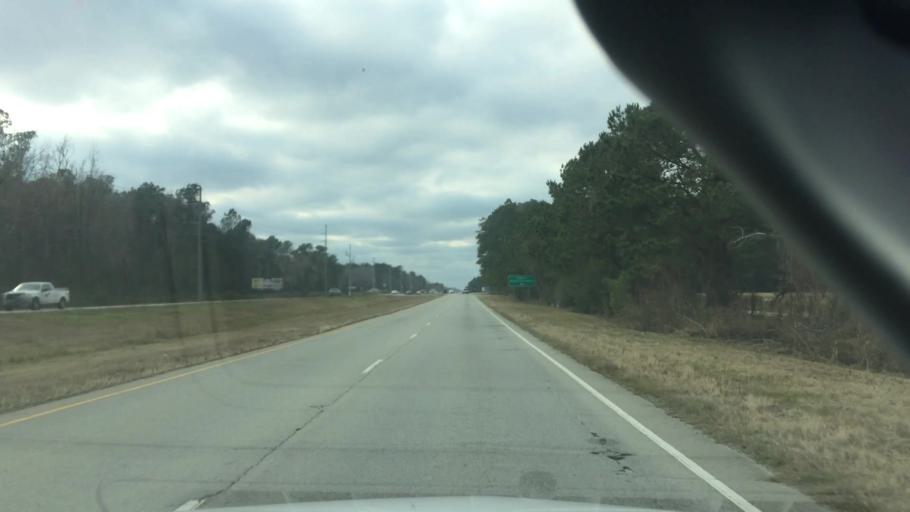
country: US
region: North Carolina
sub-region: Brunswick County
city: Shallotte
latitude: 33.9556
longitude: -78.4430
